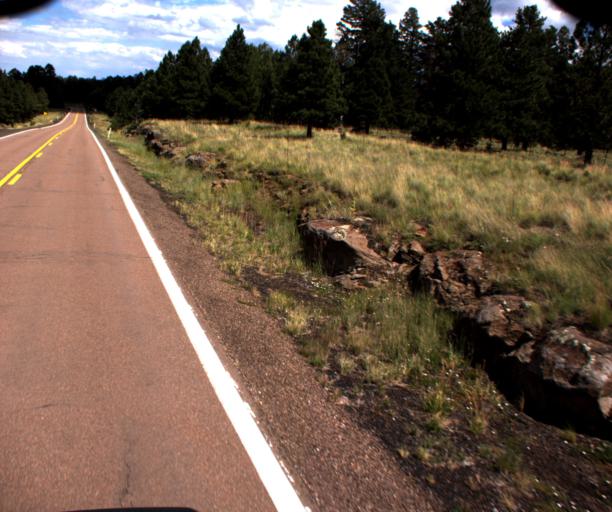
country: US
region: Arizona
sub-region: Apache County
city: Eagar
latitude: 34.0563
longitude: -109.5054
